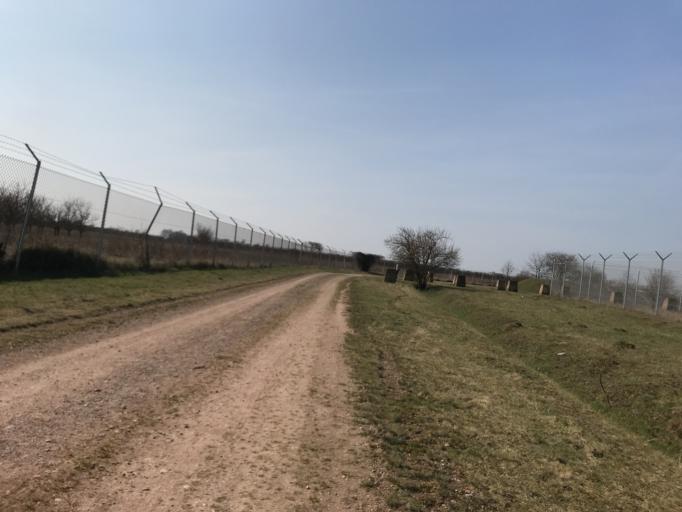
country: DE
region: Rheinland-Pfalz
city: Wackernheim
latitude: 49.9627
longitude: 8.1450
